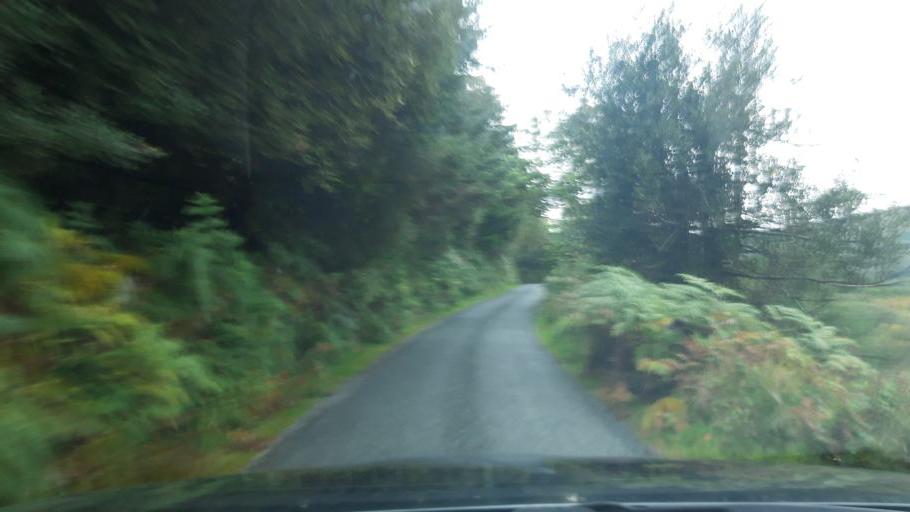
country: IE
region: Leinster
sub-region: Wicklow
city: Enniskerry
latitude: 53.1756
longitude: -6.2546
